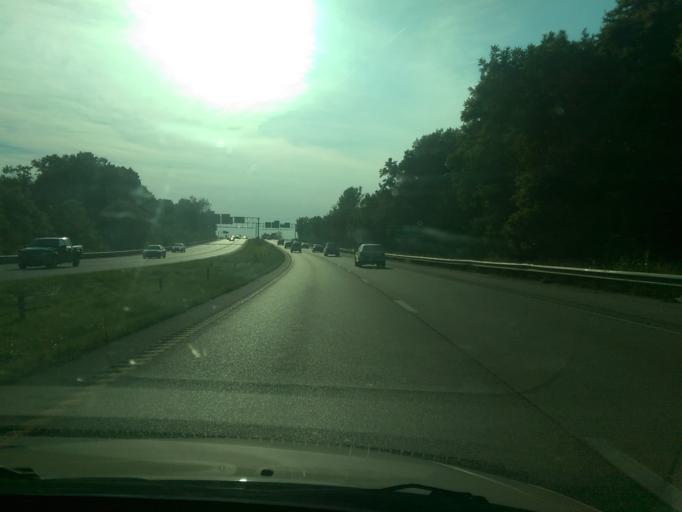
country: US
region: Missouri
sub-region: Clay County
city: Gladstone
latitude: 39.1789
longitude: -94.5679
